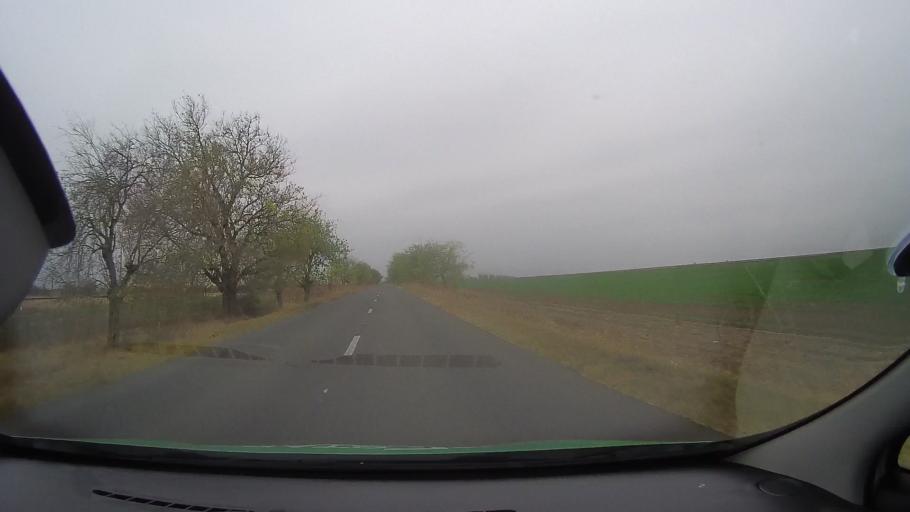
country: RO
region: Ialomita
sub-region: Comuna Valea Ciorii
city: Valea Ciorii
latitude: 44.6945
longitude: 27.6032
